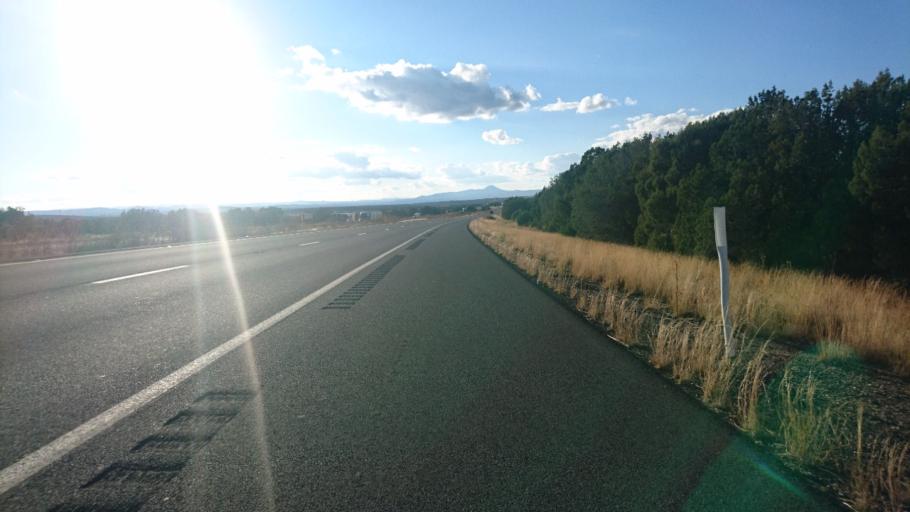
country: US
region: Arizona
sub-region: Coconino County
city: Williams
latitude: 35.2135
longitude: -112.4098
